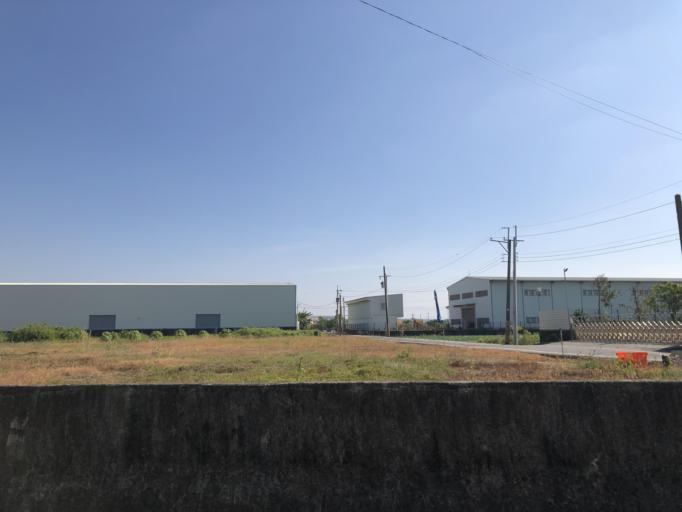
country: TW
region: Taiwan
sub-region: Tainan
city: Tainan
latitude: 23.0114
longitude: 120.2875
